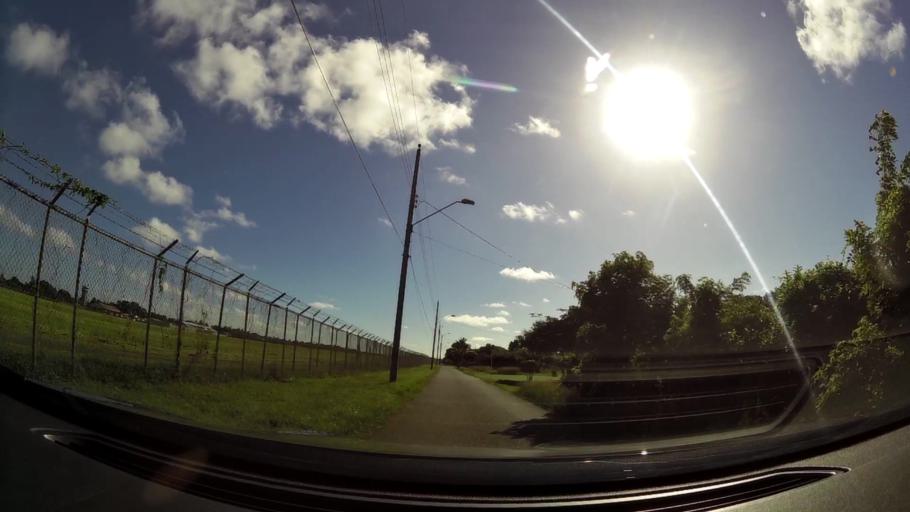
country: TT
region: Tobago
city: Scarborough
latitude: 11.1492
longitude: -60.8353
